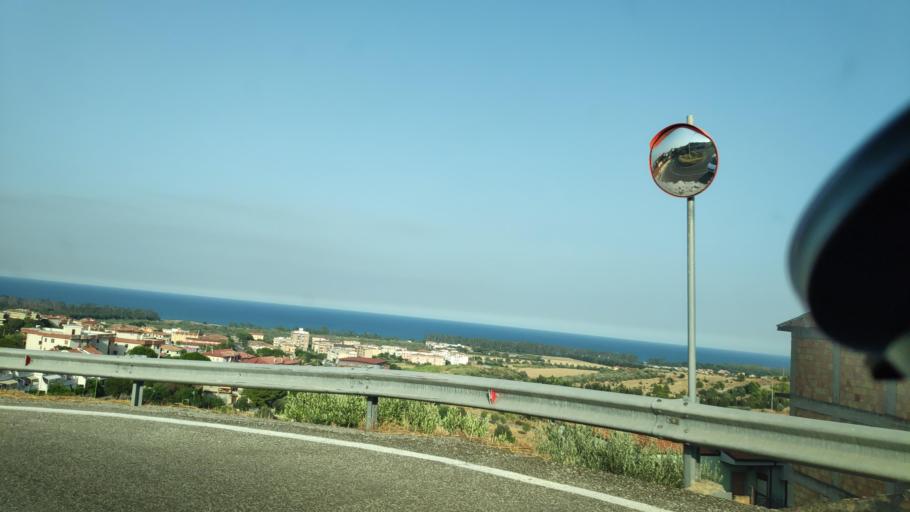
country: IT
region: Calabria
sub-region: Provincia di Catanzaro
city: Sant'Andrea Ionio Marina
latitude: 38.6184
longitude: 16.5431
